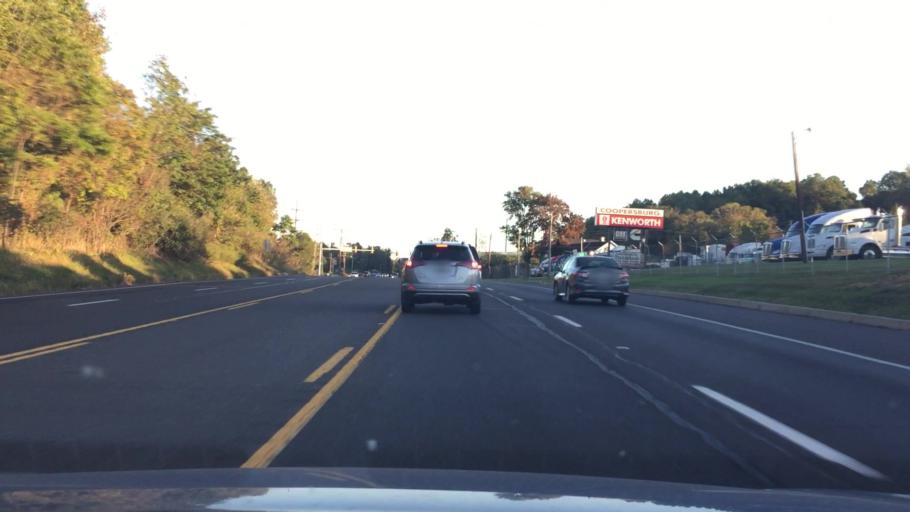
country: US
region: Pennsylvania
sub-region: Lehigh County
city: Coopersburg
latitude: 40.5010
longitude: -75.3859
